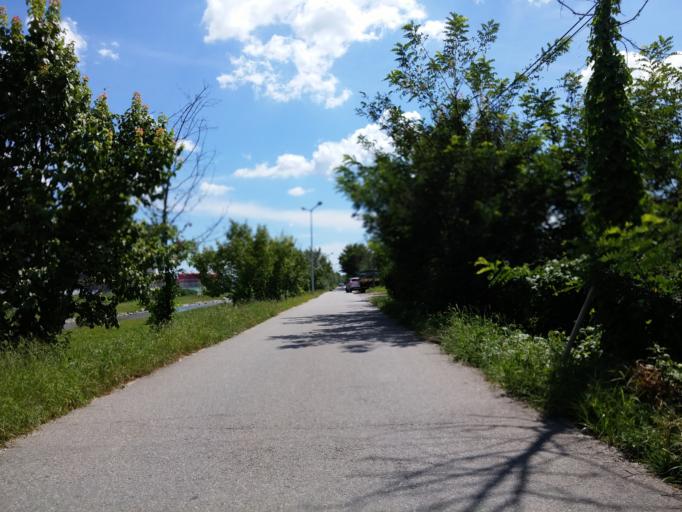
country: KR
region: Chungcheongbuk-do
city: Cheongju-si
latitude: 36.6056
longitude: 127.4972
